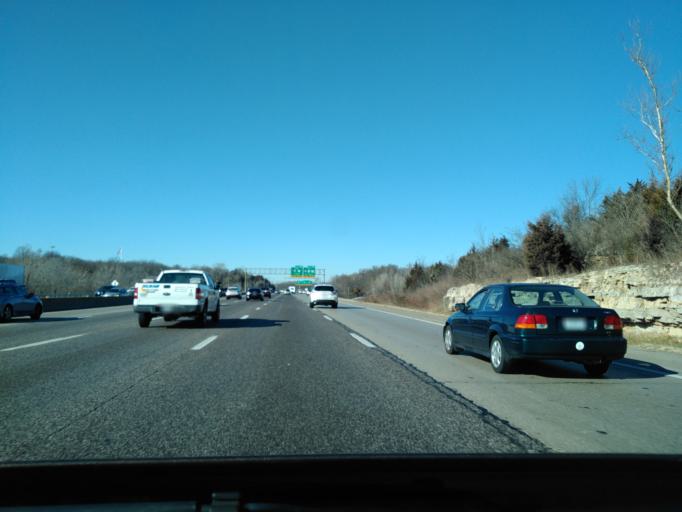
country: US
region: Missouri
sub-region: Saint Louis County
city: Sunset Hills
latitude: 38.5405
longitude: -90.4182
